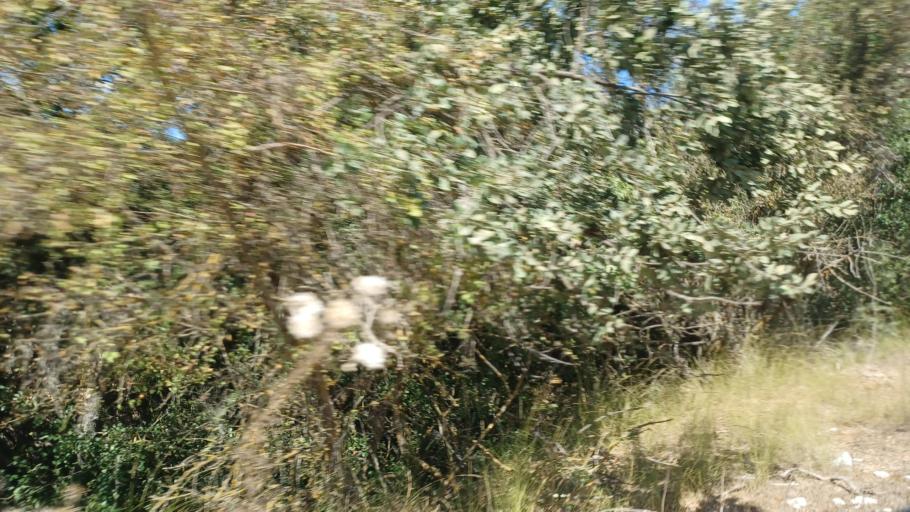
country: CY
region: Pafos
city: Mesogi
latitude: 34.8420
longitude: 32.5147
